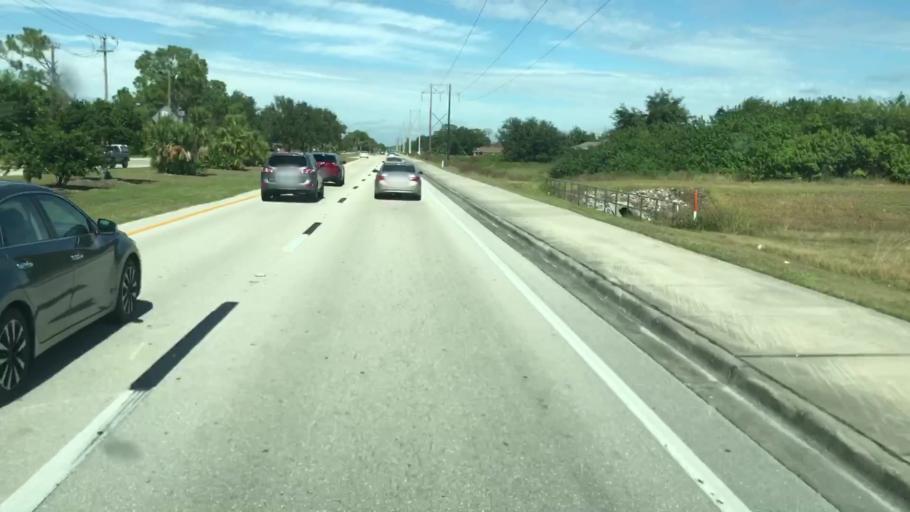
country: US
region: Florida
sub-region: Lee County
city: Gateway
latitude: 26.5985
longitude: -81.7129
